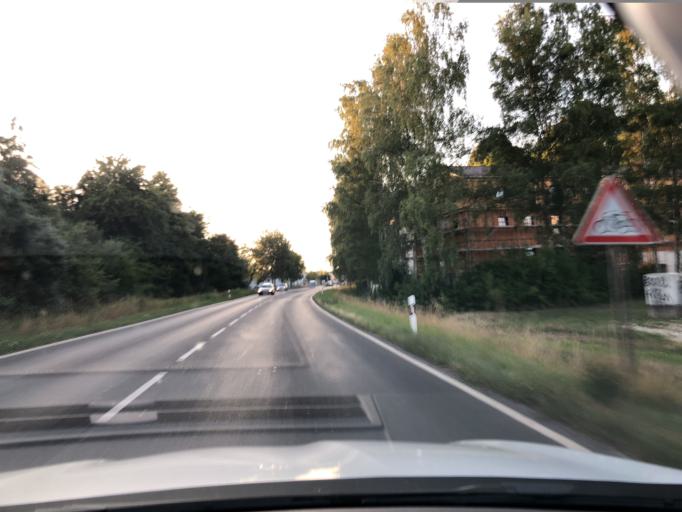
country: DE
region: Bavaria
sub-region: Upper Palatinate
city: Sulzbach-Rosenberg
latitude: 49.4934
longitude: 11.7584
